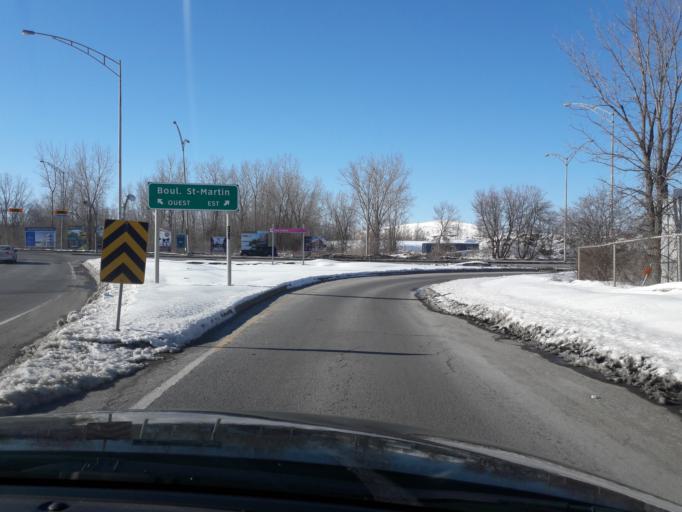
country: CA
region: Quebec
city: Dollard-Des Ormeaux
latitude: 45.5422
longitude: -73.7925
